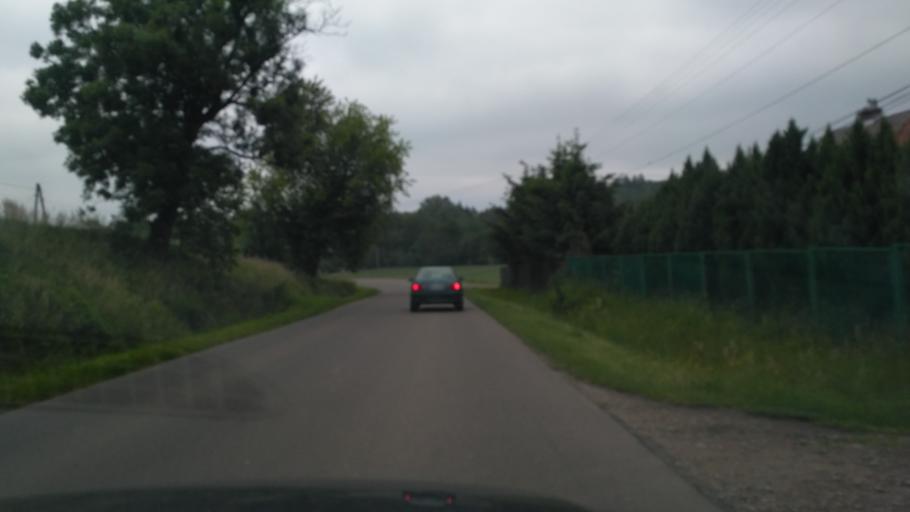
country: PL
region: Subcarpathian Voivodeship
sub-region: Powiat ropczycko-sedziszowski
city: Sedziszow Malopolski
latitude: 50.0429
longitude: 21.7000
